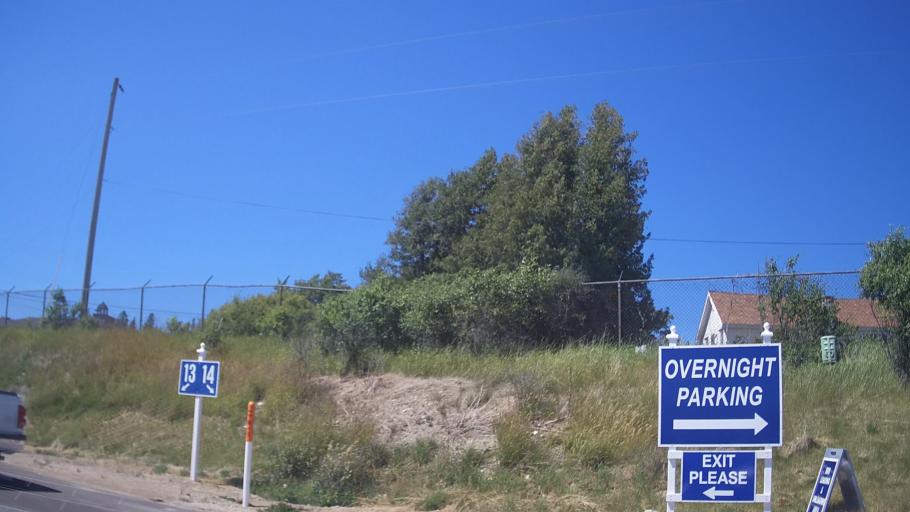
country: US
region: Michigan
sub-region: Mackinac County
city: Saint Ignace
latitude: 45.8750
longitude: -84.7277
